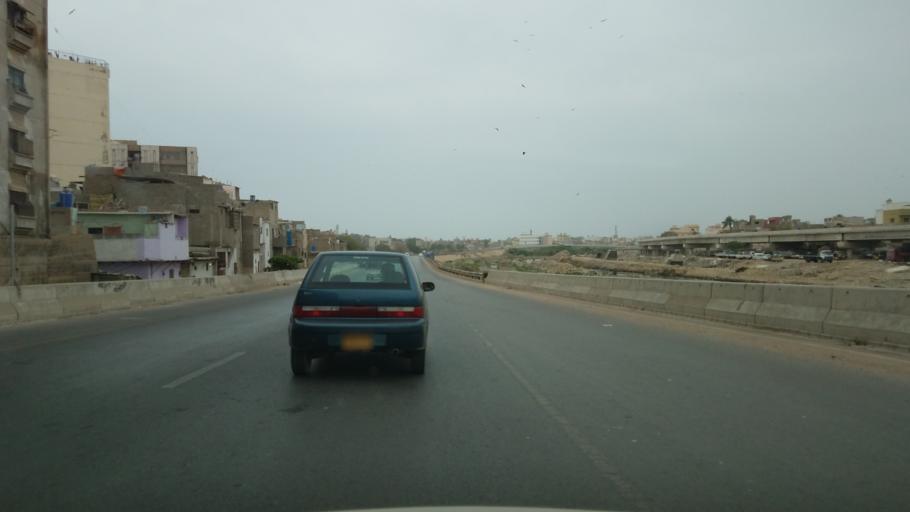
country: PK
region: Sindh
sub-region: Karachi District
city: Karachi
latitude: 24.8812
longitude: 67.0191
